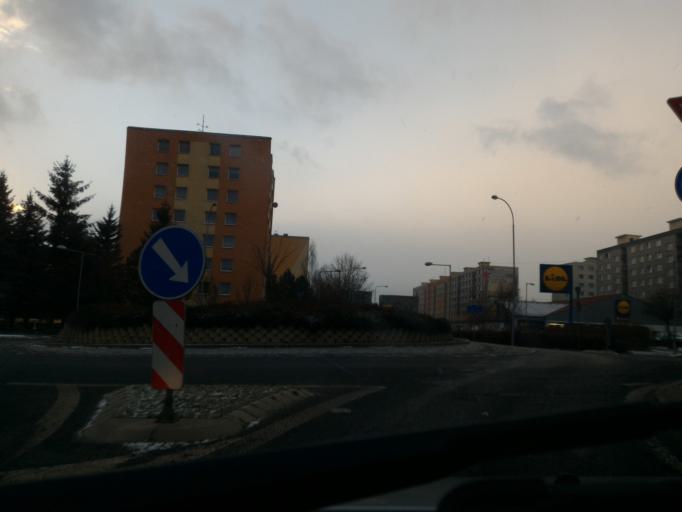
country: CZ
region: Ustecky
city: Varnsdorf
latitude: 50.9086
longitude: 14.6182
